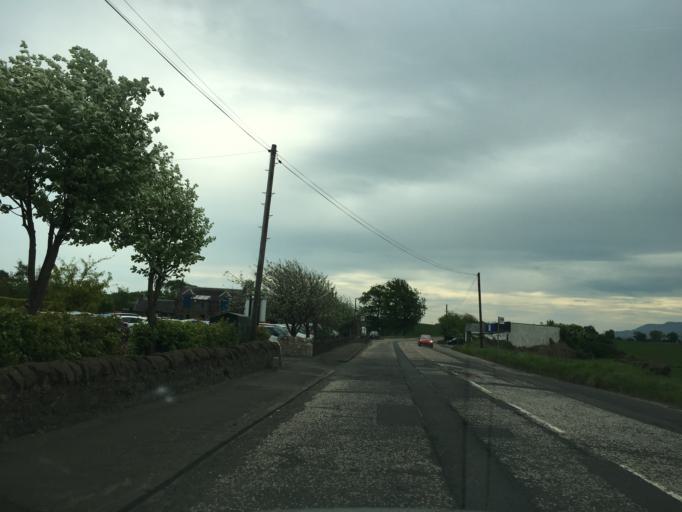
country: GB
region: Scotland
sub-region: Edinburgh
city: Ratho
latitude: 55.9501
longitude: -3.3359
